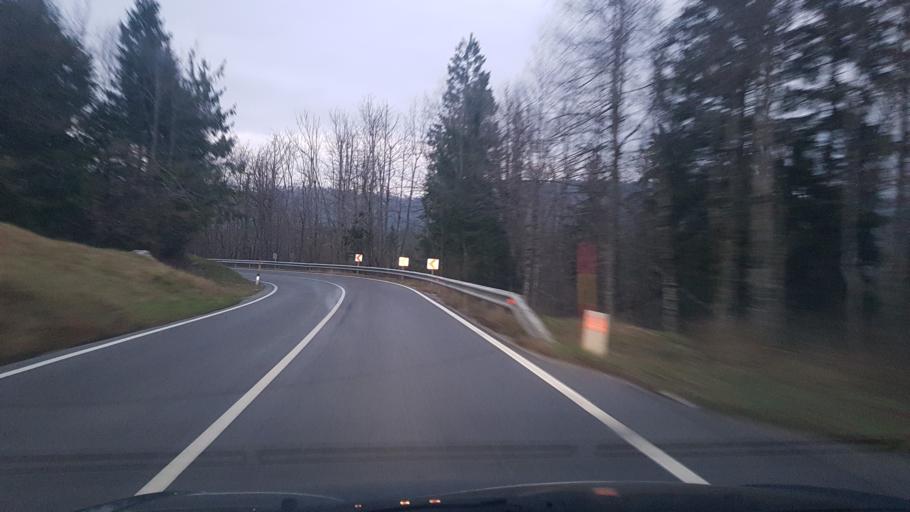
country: SI
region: Idrija
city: Idrija
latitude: 45.9516
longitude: 14.0794
